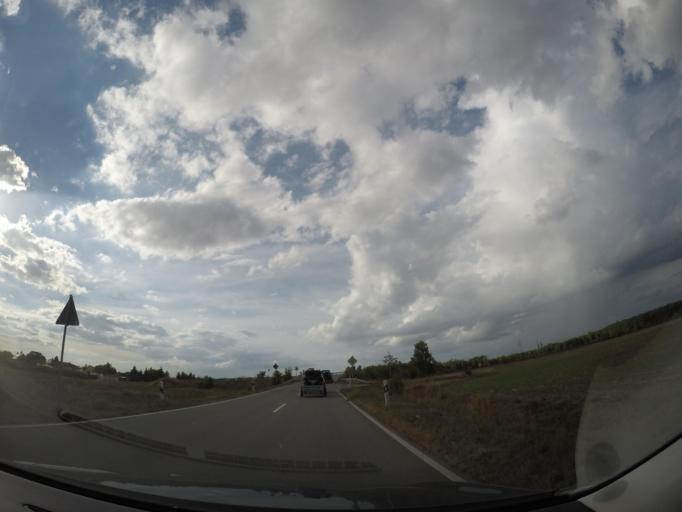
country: DE
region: Saxony-Anhalt
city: Mieste
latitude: 52.4883
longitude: 11.2396
